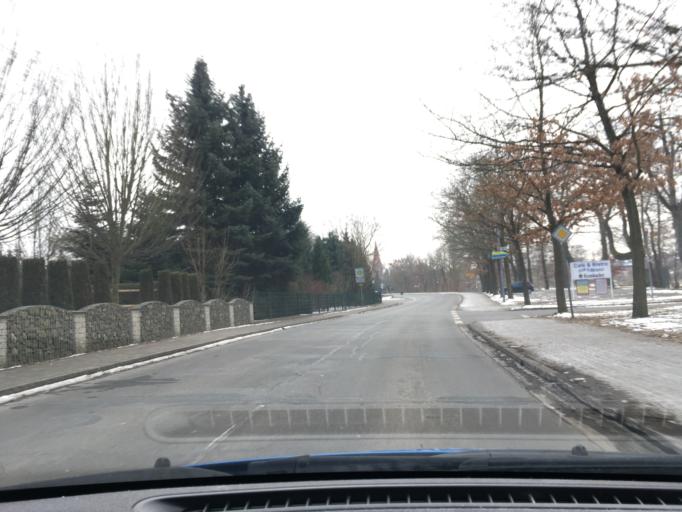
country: DE
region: Lower Saxony
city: Bienenbuttel
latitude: 53.1457
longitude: 10.4914
